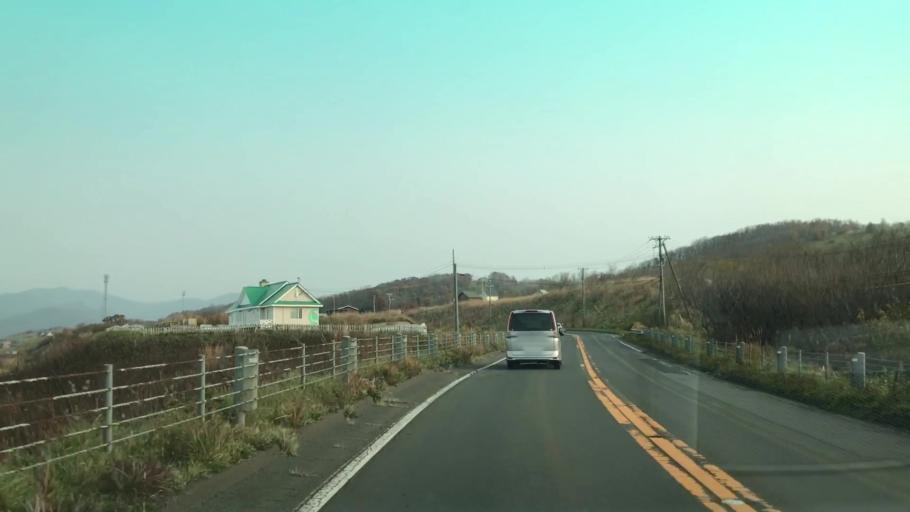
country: JP
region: Hokkaido
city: Ishikari
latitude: 43.3837
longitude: 141.4313
